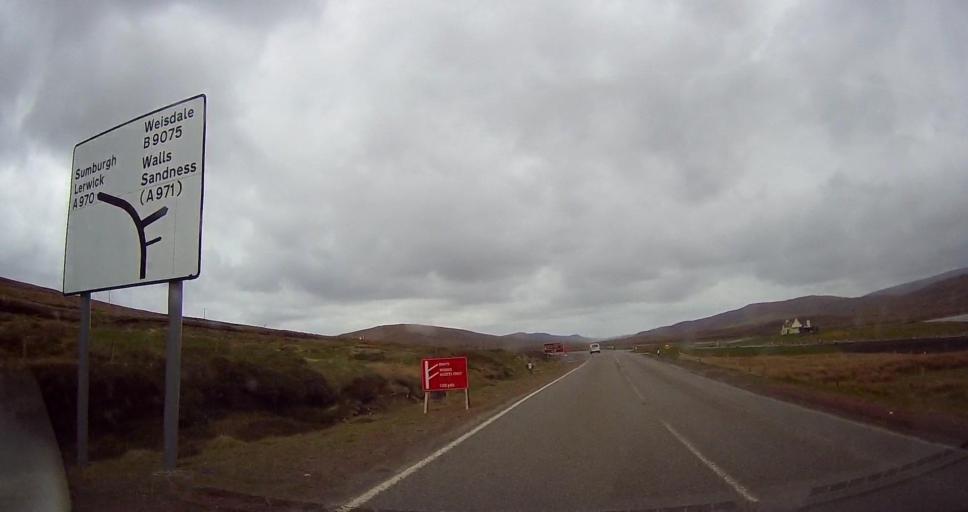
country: GB
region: Scotland
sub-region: Shetland Islands
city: Lerwick
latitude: 60.2813
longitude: -1.2440
